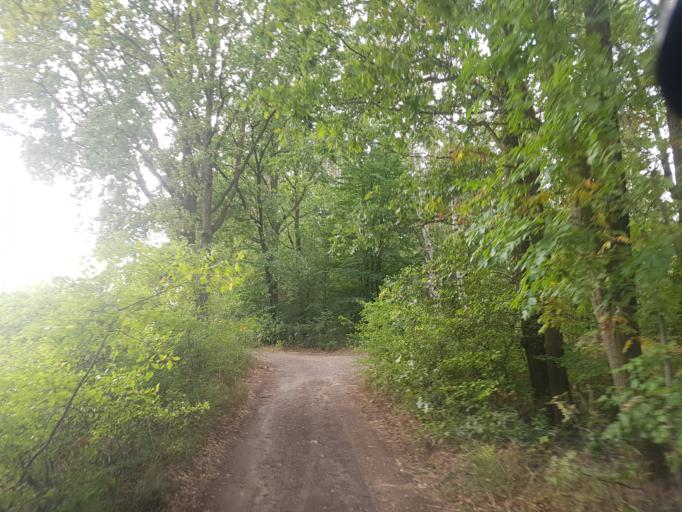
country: DE
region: Brandenburg
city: Calau
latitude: 51.7226
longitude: 13.9414
